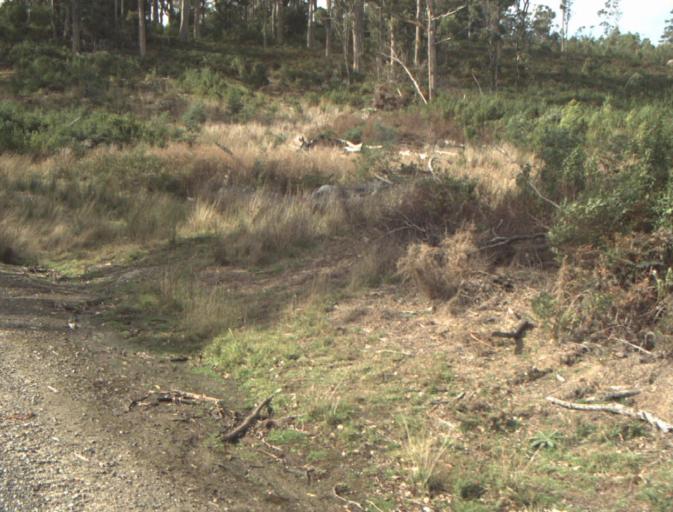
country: AU
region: Tasmania
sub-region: Launceston
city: Mayfield
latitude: -41.1863
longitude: 147.1913
